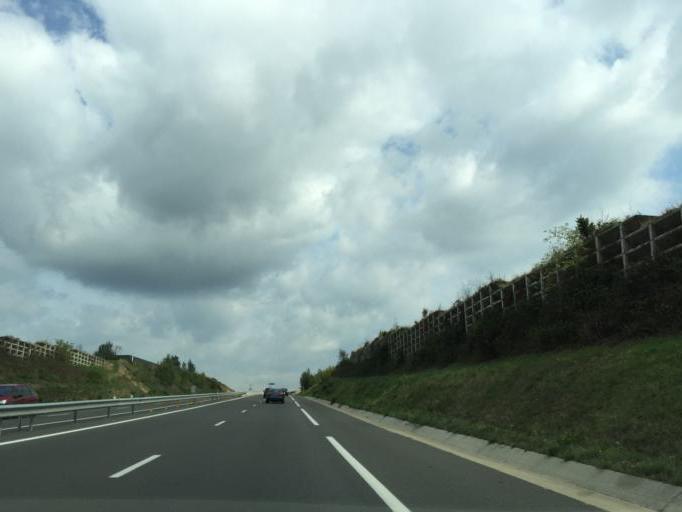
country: FR
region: Rhone-Alpes
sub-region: Departement de la Loire
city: Andrezieux-Boutheon
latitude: 45.5173
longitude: 4.2559
